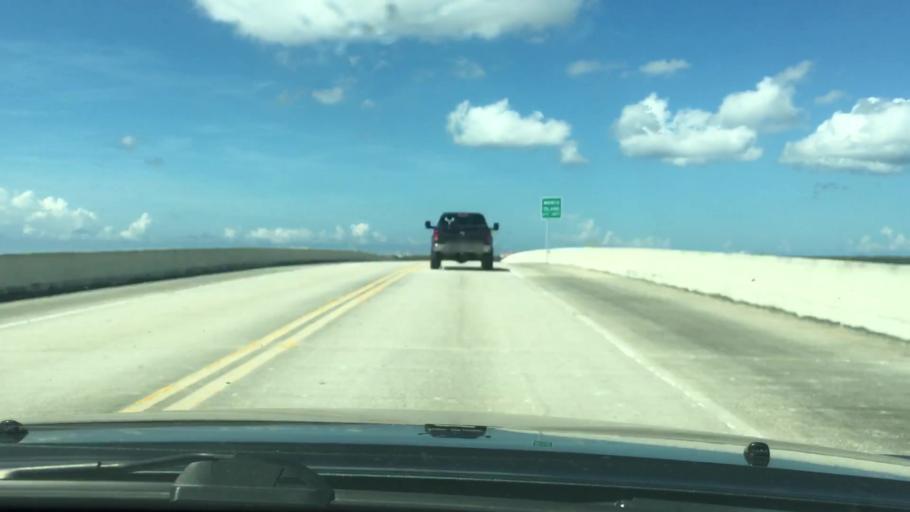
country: US
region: Florida
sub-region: Collier County
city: Marco
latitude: 25.9328
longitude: -81.6529
